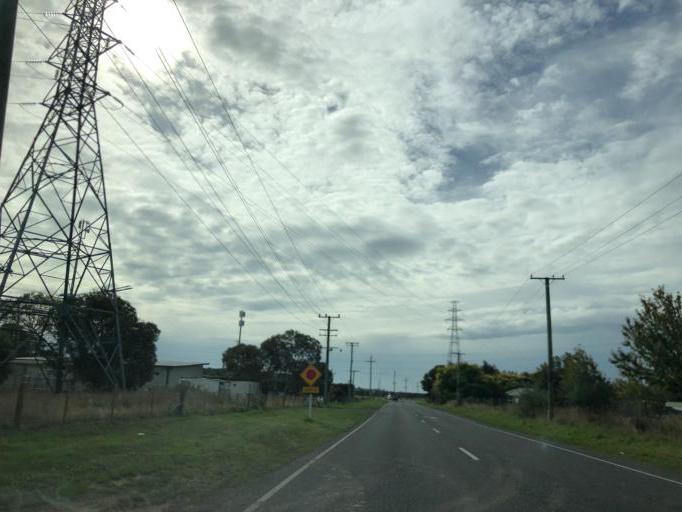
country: NZ
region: Canterbury
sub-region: Selwyn District
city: Lincoln
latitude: -43.6379
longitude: 172.4512
